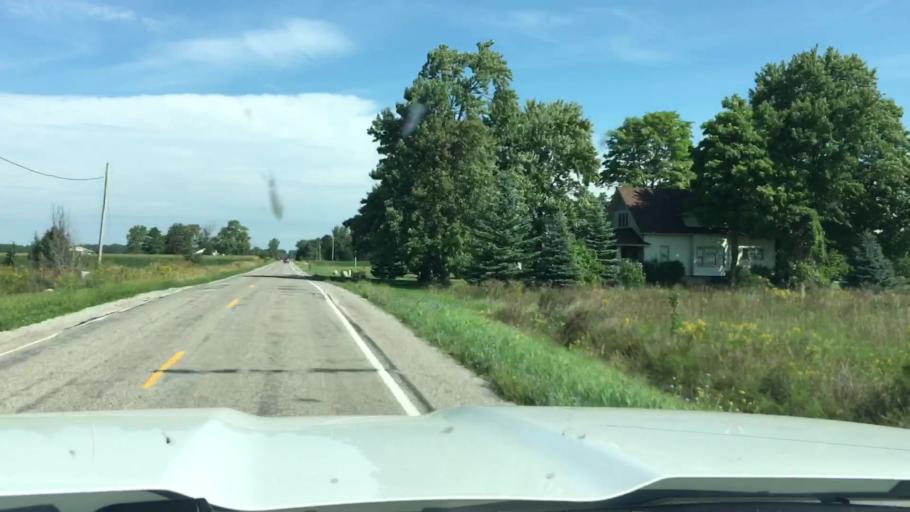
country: US
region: Michigan
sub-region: Saginaw County
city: Hemlock
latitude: 43.4369
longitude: -84.2300
